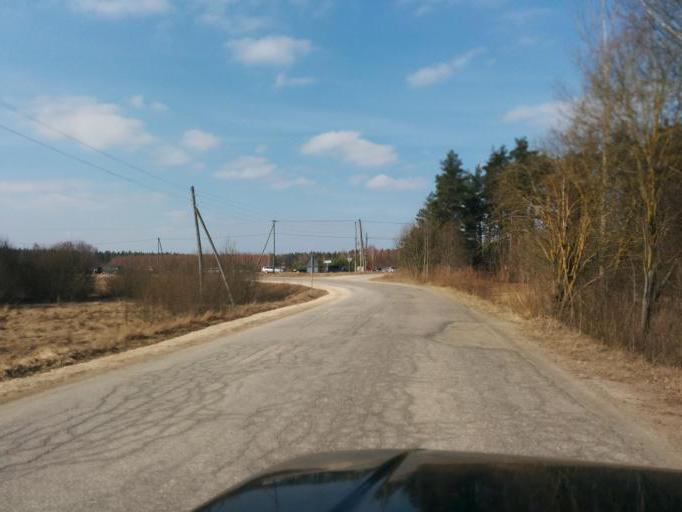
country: LV
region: Kekava
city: Kekava
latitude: 56.8495
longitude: 24.2410
